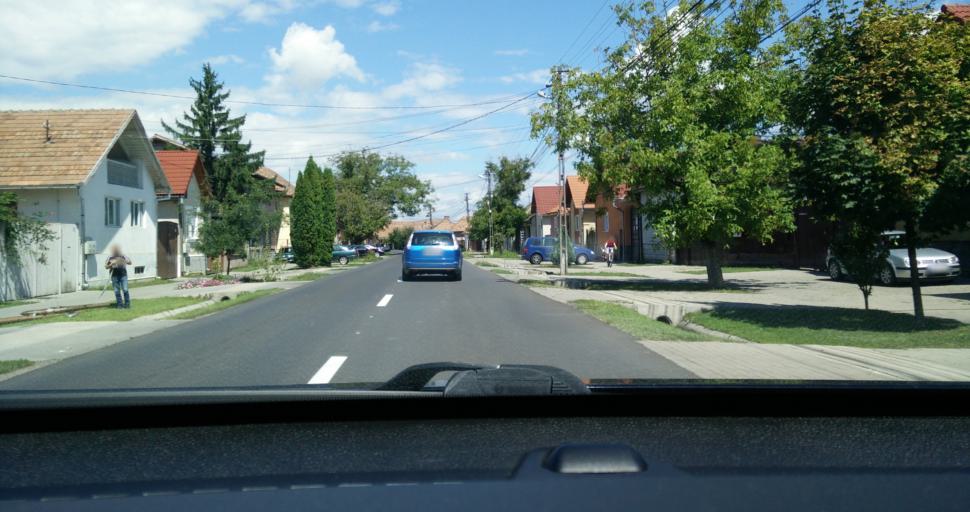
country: RO
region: Alba
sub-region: Municipiul Sebes
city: Petresti
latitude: 45.9233
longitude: 23.5623
